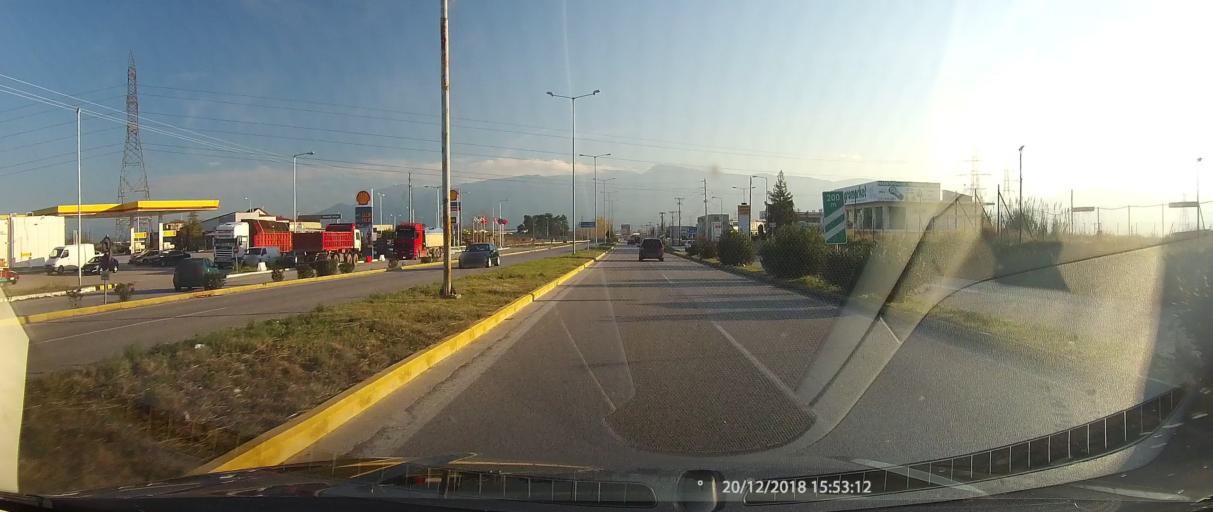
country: GR
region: Central Greece
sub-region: Nomos Fthiotidos
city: Rodhitsa
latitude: 38.8752
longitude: 22.4551
